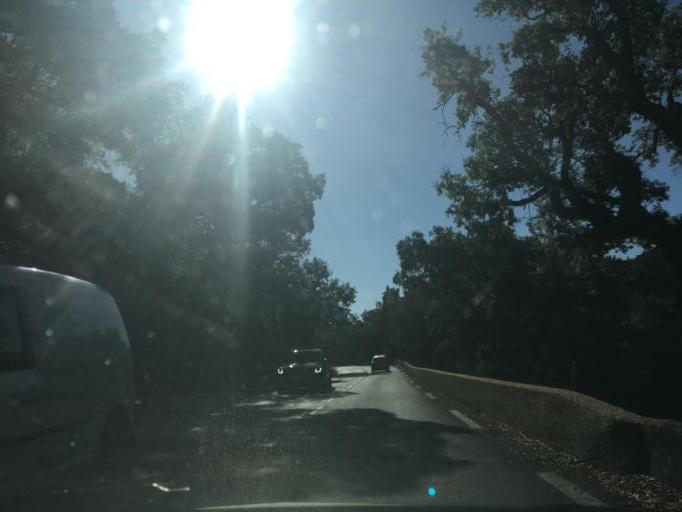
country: FR
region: Provence-Alpes-Cote d'Azur
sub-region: Departement du Var
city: La Garde-Freinet
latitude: 43.3292
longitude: 6.4677
